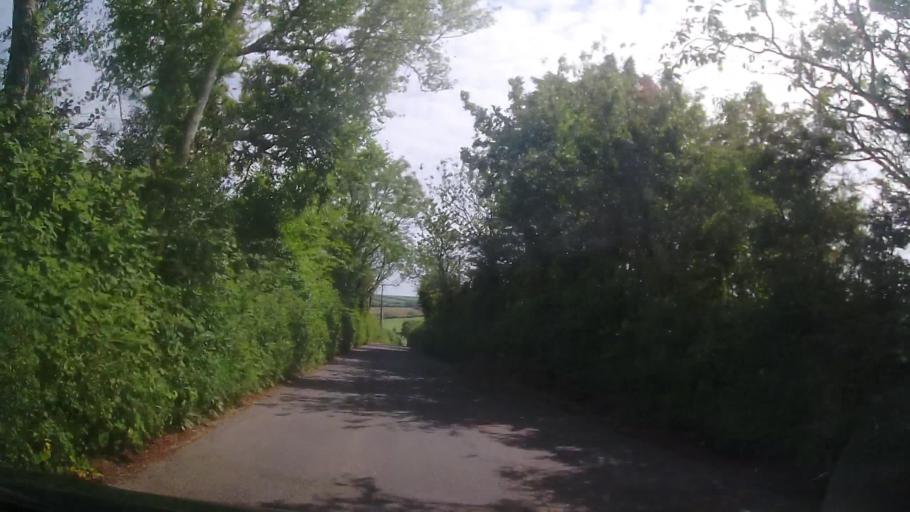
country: GB
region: England
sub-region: Devon
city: Salcombe
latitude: 50.2645
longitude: -3.6773
